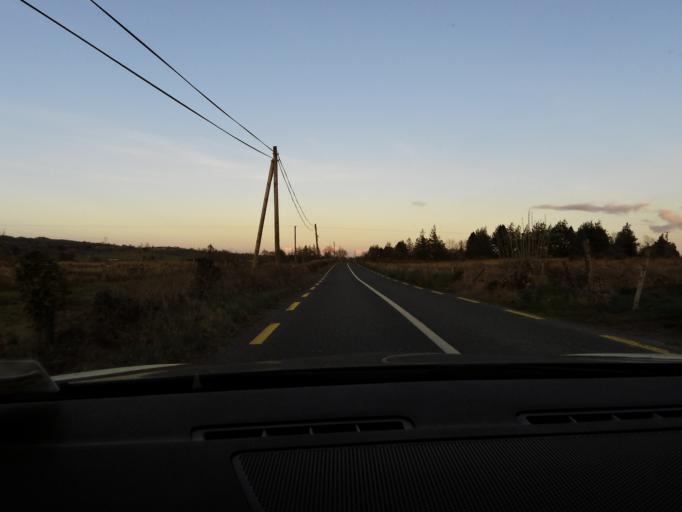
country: IE
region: Connaught
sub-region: Roscommon
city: Boyle
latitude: 53.9714
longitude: -8.4040
